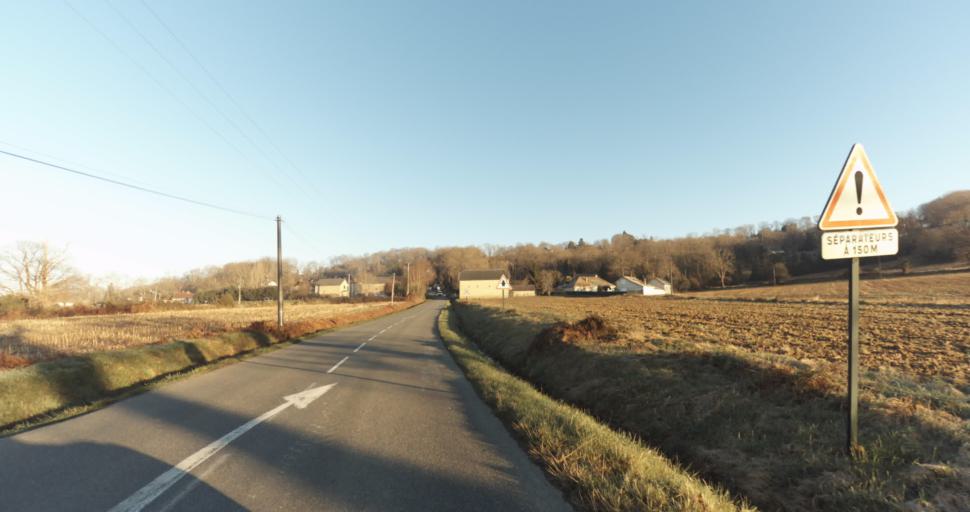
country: FR
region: Aquitaine
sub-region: Departement des Pyrenees-Atlantiques
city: Morlaas
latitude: 43.3261
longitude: -0.2734
